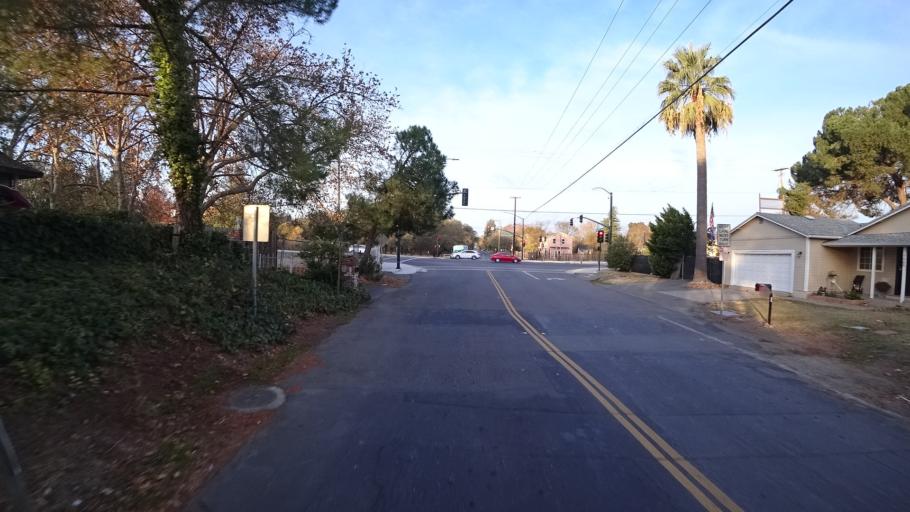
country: US
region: California
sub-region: Sacramento County
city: Citrus Heights
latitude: 38.7186
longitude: -121.2711
